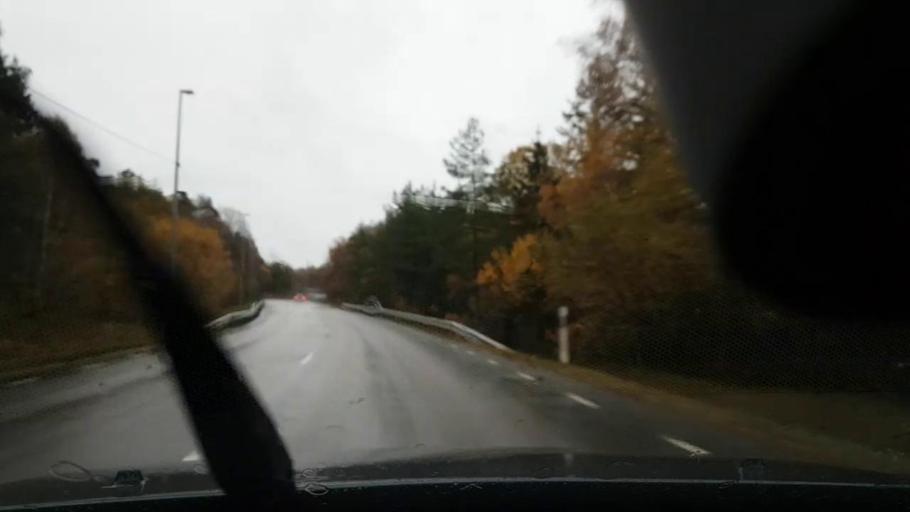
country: SE
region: Vaestra Goetaland
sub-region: Molndal
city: Kallered
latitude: 57.6027
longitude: 12.0733
